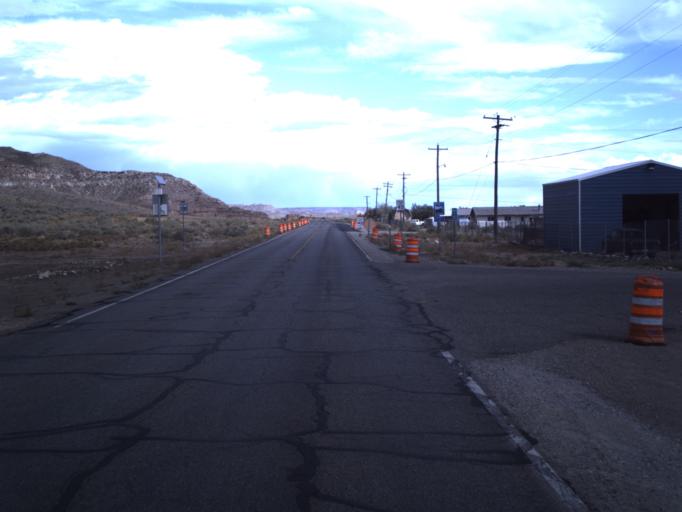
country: US
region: Utah
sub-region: San Juan County
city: Blanding
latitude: 37.2596
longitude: -109.3001
